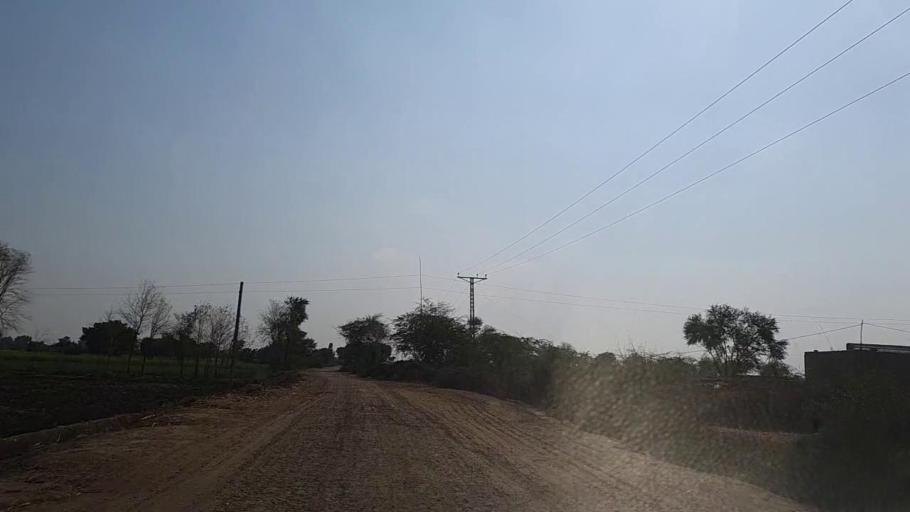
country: PK
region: Sindh
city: Daur
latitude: 26.4519
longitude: 68.2346
